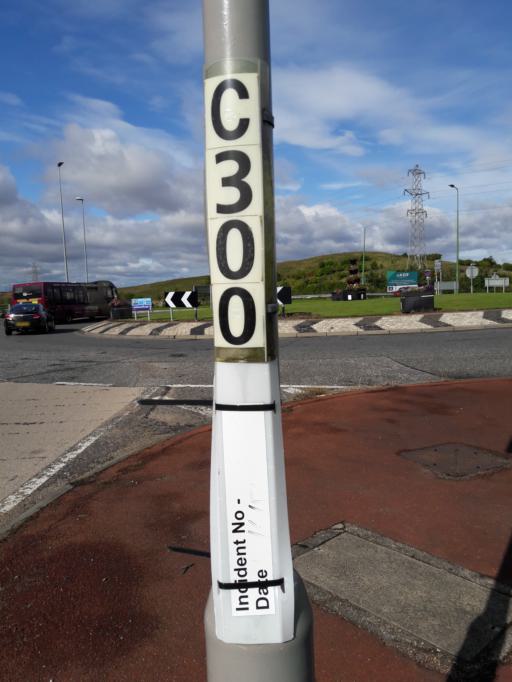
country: GB
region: England
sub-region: County Durham
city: Hawthorn
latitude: 54.8125
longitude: -1.3636
